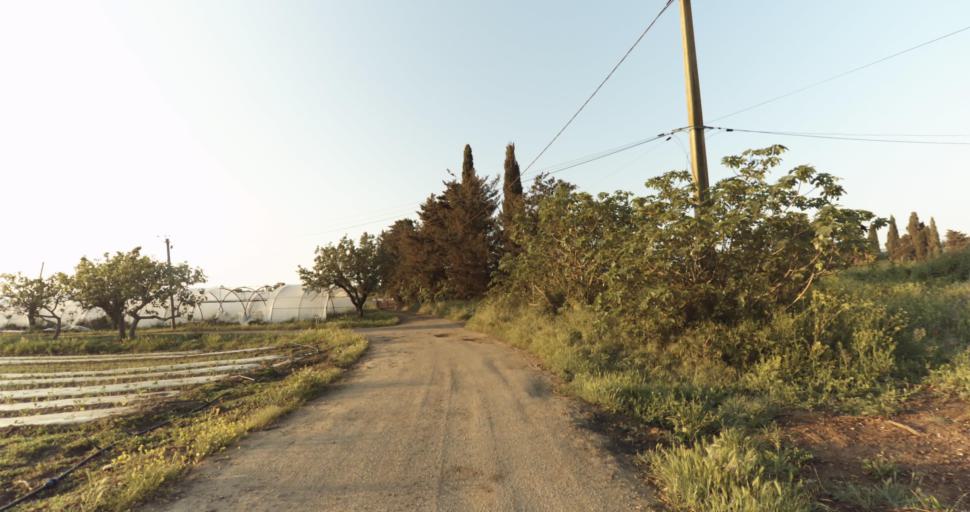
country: FR
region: Corsica
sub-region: Departement de la Haute-Corse
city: Biguglia
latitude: 42.5998
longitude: 9.4564
